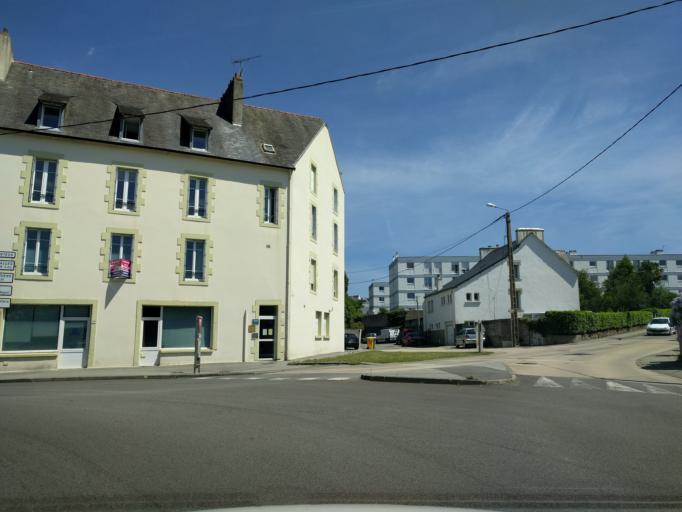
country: FR
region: Brittany
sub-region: Departement du Finistere
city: Quimper
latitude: 48.0023
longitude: -4.1081
